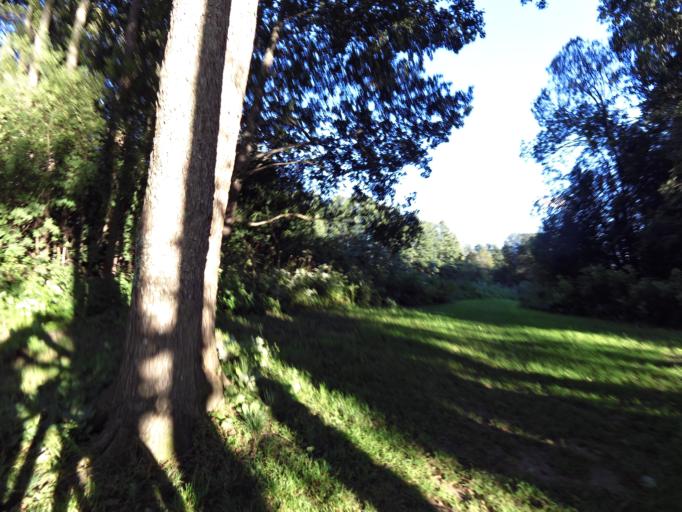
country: SE
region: Gaevleborg
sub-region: Gavle Kommun
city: Gavle
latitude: 60.7167
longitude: 17.1492
